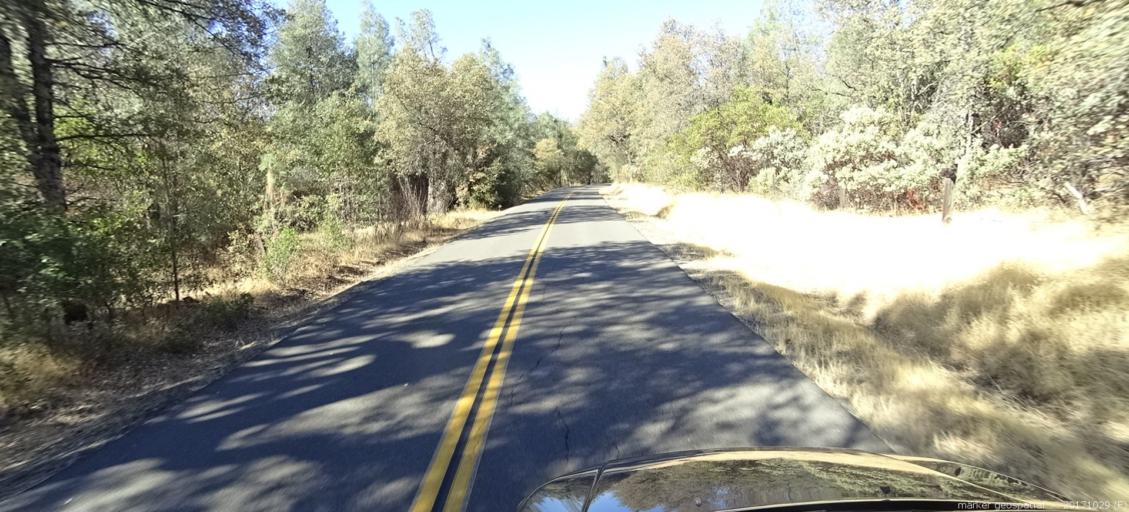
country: US
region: California
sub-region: Shasta County
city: Shasta
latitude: 40.4785
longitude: -122.6494
